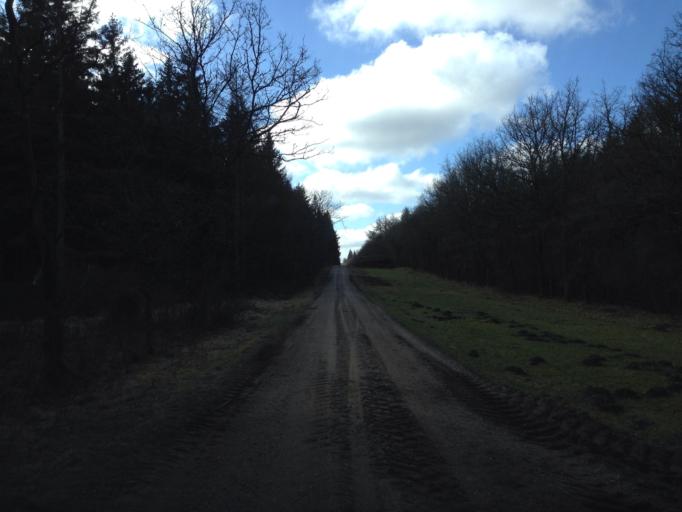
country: DK
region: Central Jutland
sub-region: Holstebro Kommune
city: Ulfborg
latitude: 56.2724
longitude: 8.4638
